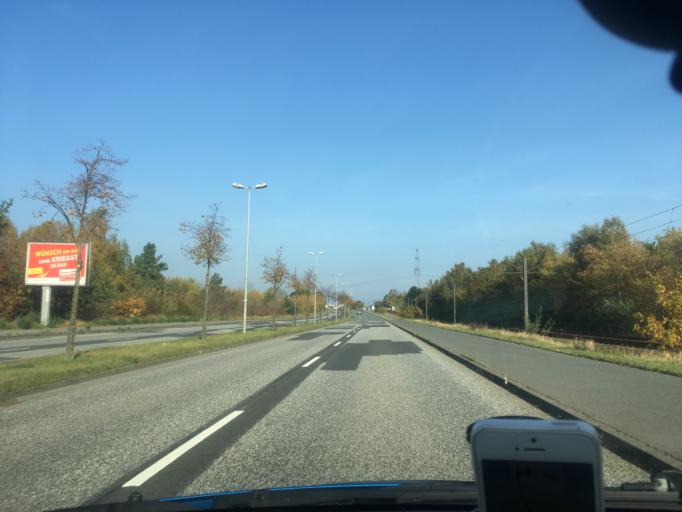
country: DE
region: Mecklenburg-Vorpommern
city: Feldstadt
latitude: 53.5800
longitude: 11.3989
